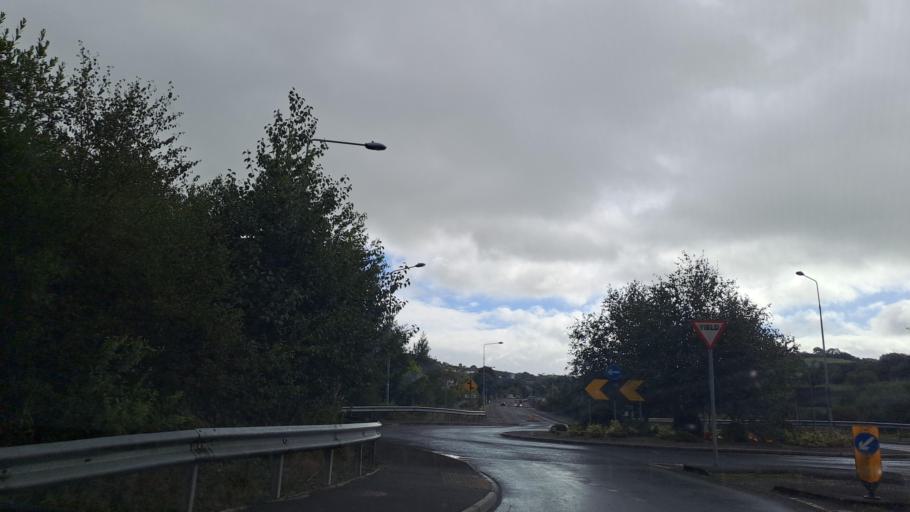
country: IE
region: Ulster
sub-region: An Cabhan
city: Bailieborough
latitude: 53.9204
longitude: -6.9703
